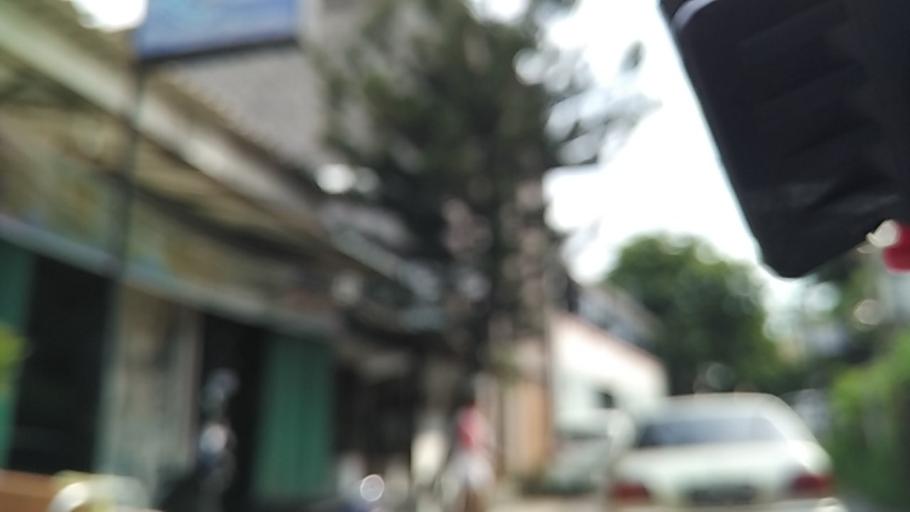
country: ID
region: Central Java
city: Semarang
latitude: -7.0004
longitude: 110.4241
